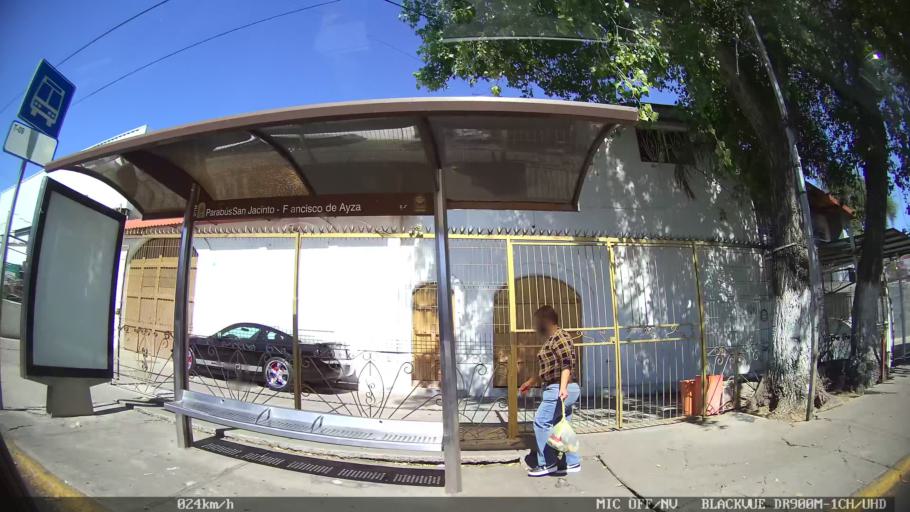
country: MX
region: Jalisco
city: Tlaquepaque
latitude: 20.6686
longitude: -103.2972
